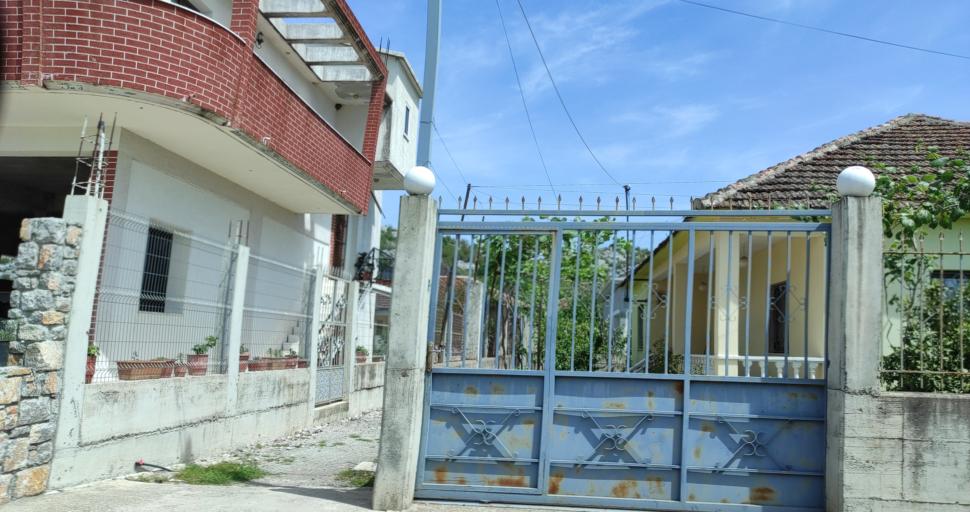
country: AL
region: Shkoder
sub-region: Rrethi i Malesia e Madhe
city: Gruemire
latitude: 42.1223
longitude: 19.5591
